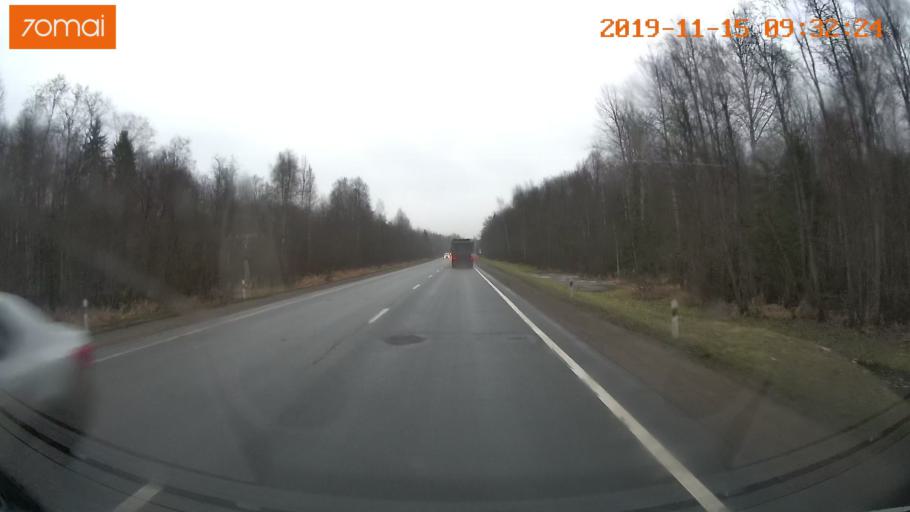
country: RU
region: Vologda
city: Sheksna
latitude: 59.2720
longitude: 38.3334
